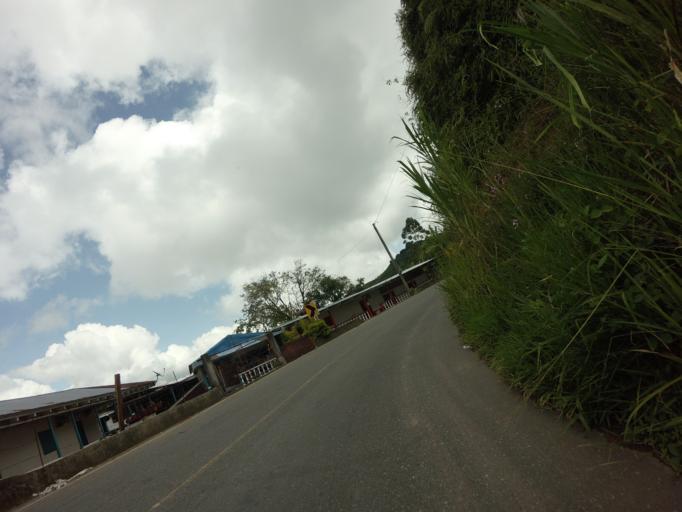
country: CO
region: Caldas
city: Marquetalia
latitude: 5.3016
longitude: -75.0192
